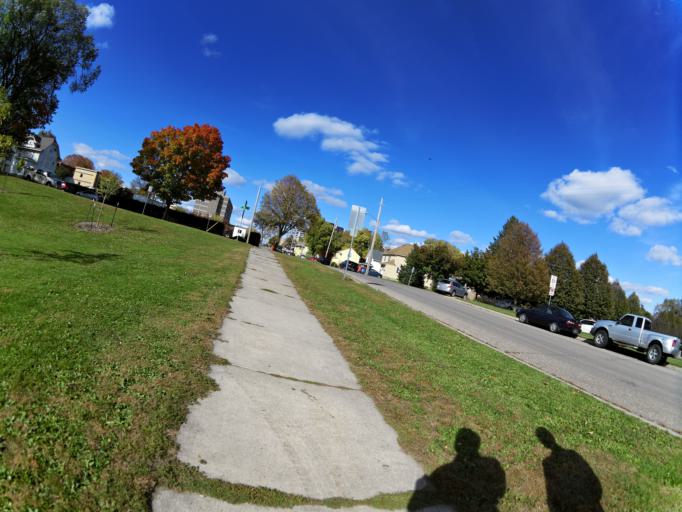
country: US
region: Minnesota
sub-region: Olmsted County
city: Rochester
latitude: 44.0163
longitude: -92.4683
